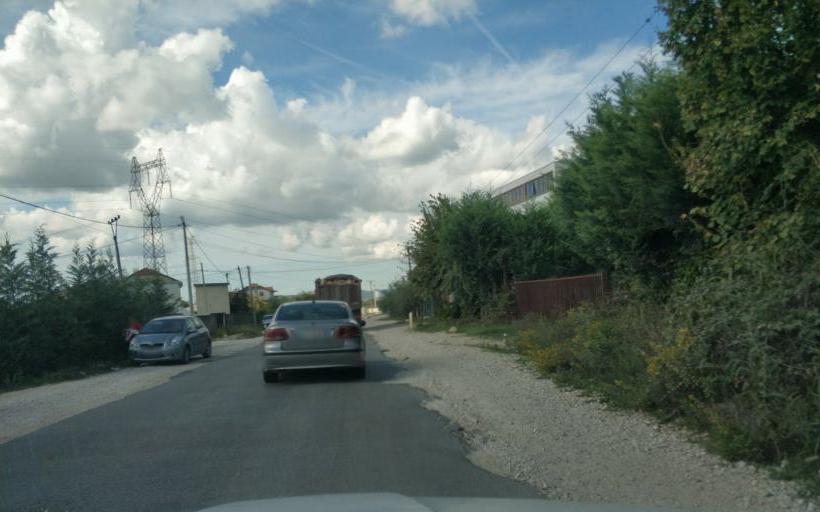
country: AL
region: Durres
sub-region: Rrethi i Krujes
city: Fushe-Kruje
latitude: 41.4768
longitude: 19.7449
